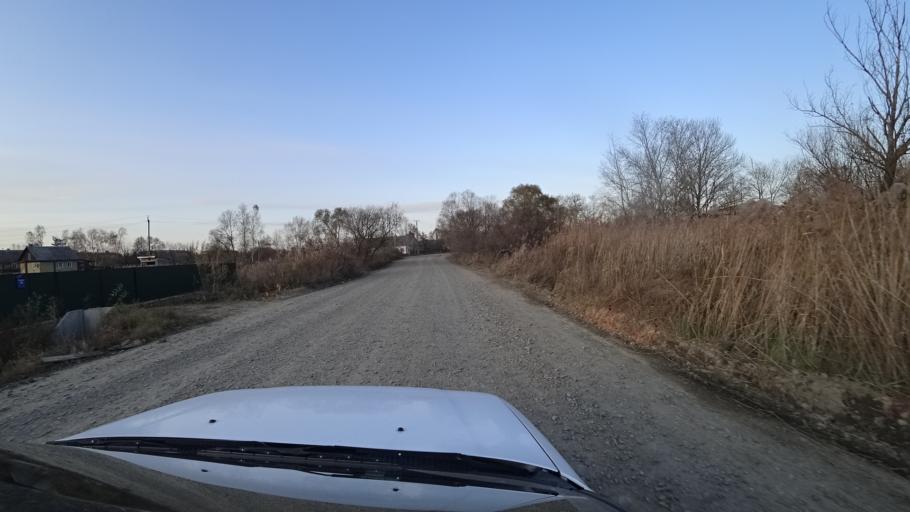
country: RU
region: Primorskiy
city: Dal'nerechensk
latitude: 45.9396
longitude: 133.8211
